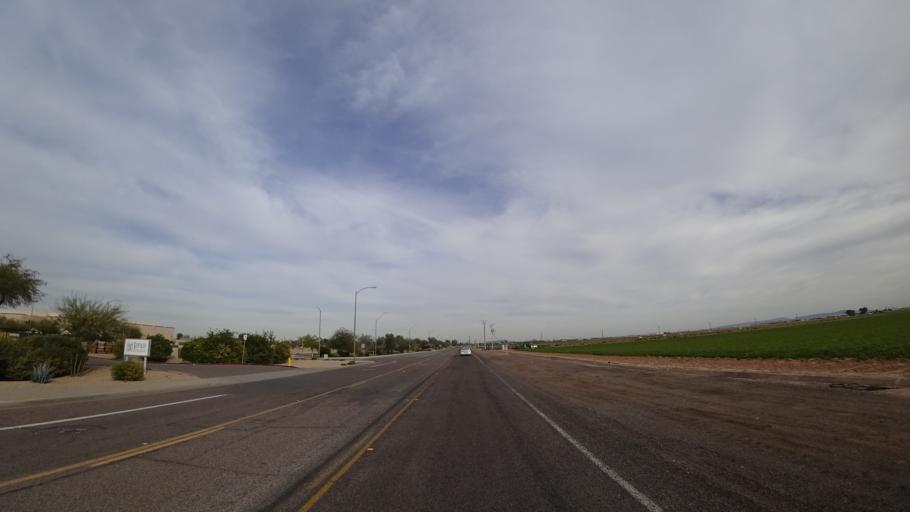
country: US
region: Arizona
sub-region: Maricopa County
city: El Mirage
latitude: 33.5801
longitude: -112.3479
